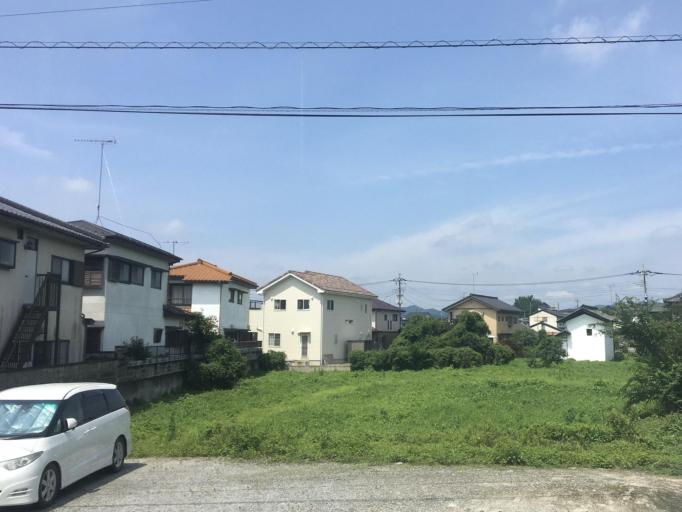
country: JP
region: Tochigi
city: Tanuma
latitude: 36.3651
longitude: 139.5809
